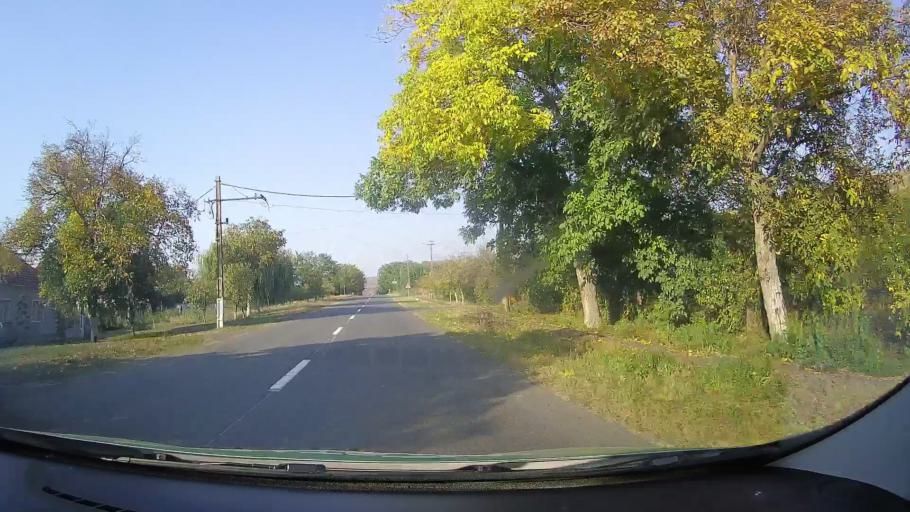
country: RO
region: Arad
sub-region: Comuna Paulis
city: Paulis
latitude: 46.1258
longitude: 21.5992
